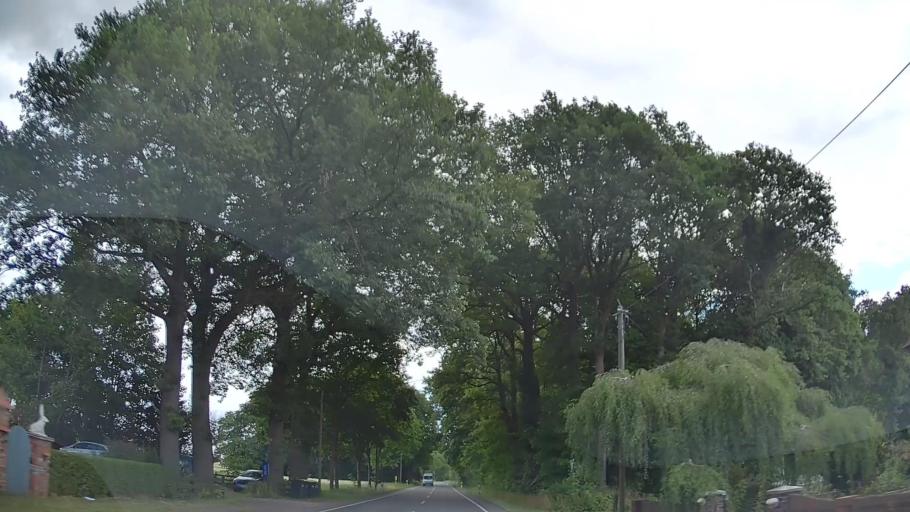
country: DE
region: Lower Saxony
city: Brockum
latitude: 52.4643
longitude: 8.4538
